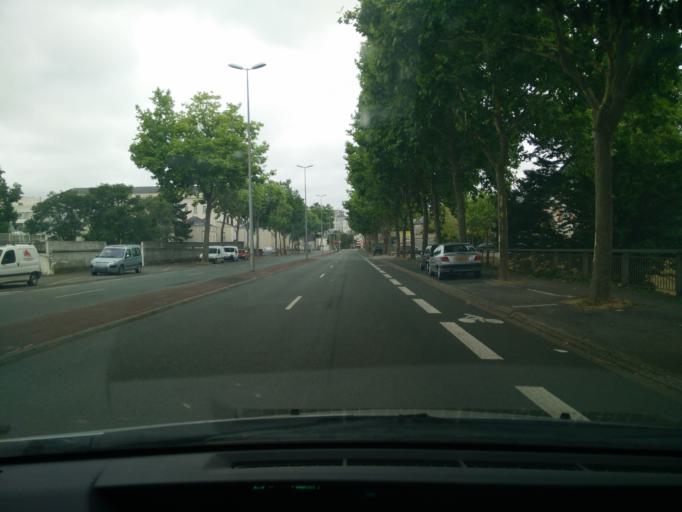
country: FR
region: Pays de la Loire
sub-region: Departement de Maine-et-Loire
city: Angers
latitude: 47.4706
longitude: -0.5360
